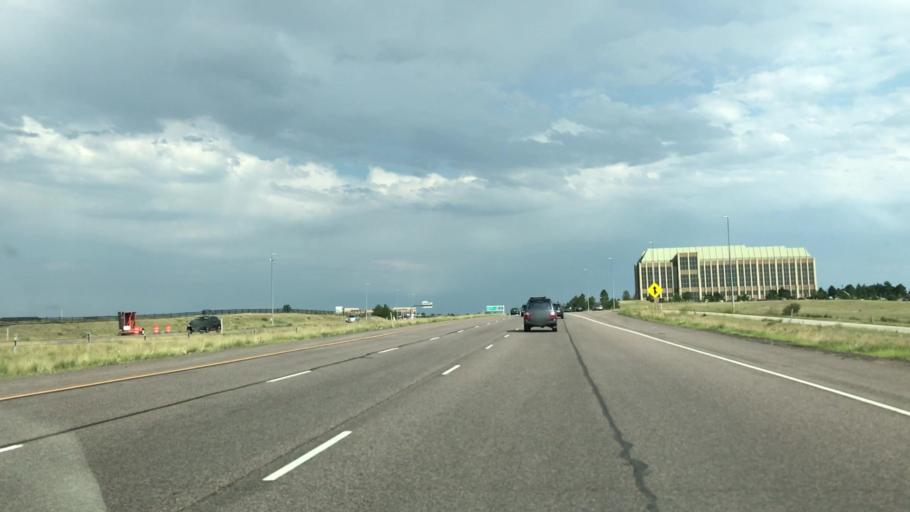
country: US
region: Colorado
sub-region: Douglas County
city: Meridian
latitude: 39.5531
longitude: -104.8601
